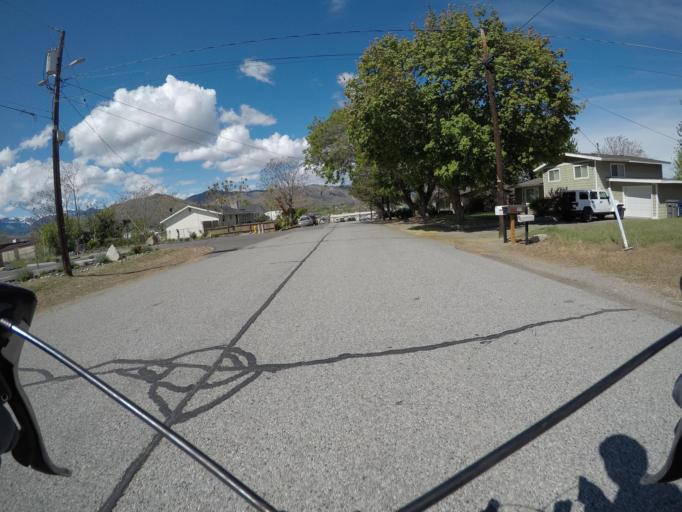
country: US
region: Washington
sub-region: Douglas County
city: East Wenatchee
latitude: 47.4037
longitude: -120.2864
